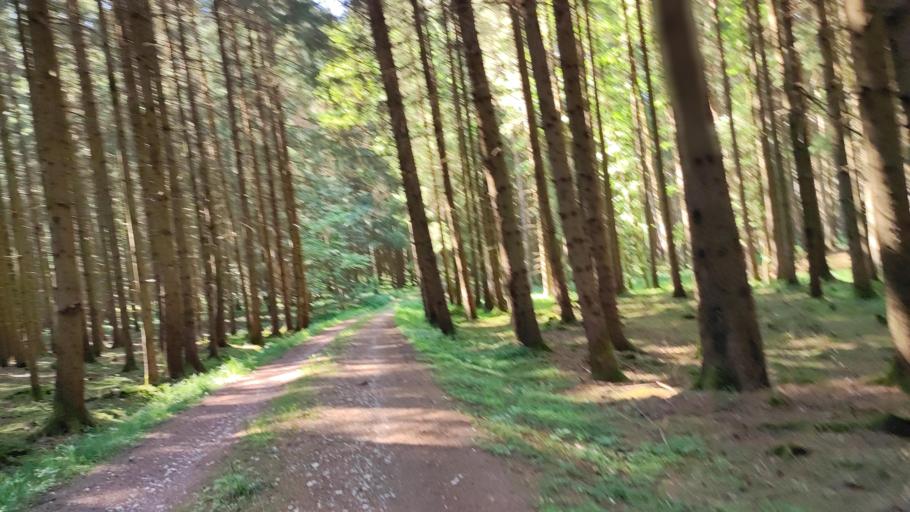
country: DE
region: Bavaria
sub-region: Swabia
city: Burtenbach
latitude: 48.3676
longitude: 10.4984
